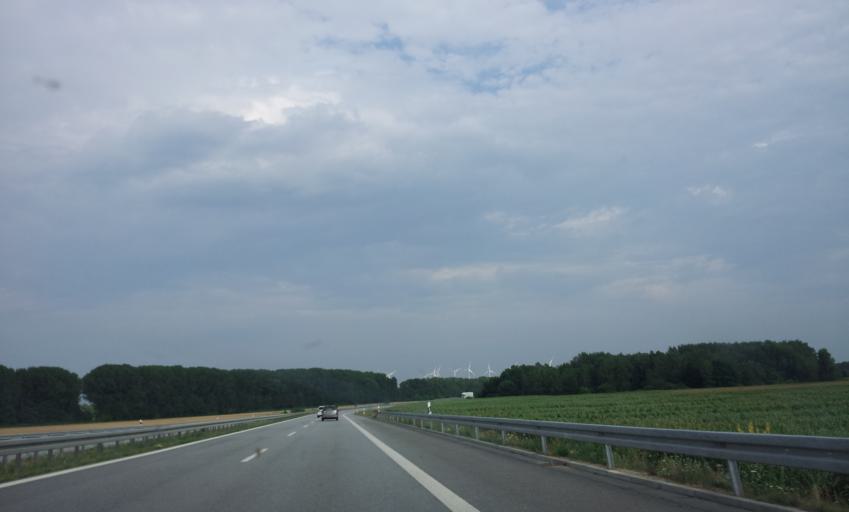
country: DE
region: Brandenburg
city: Trebbin
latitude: 52.2262
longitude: 13.2459
